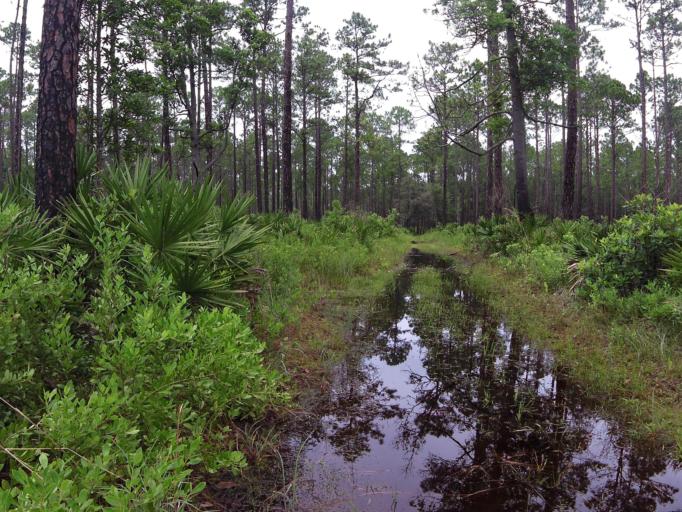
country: US
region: Florida
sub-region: Clay County
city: Green Cove Springs
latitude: 29.9630
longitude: -81.6275
